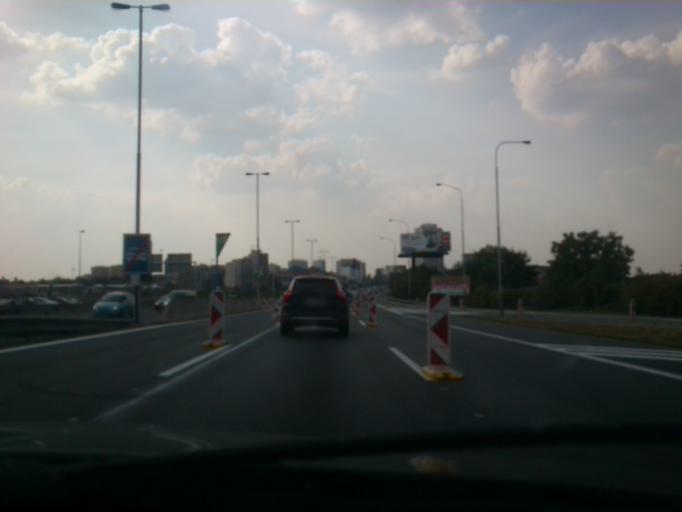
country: CZ
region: Praha
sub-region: Praha 4
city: Hodkovicky
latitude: 50.0408
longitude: 14.4685
